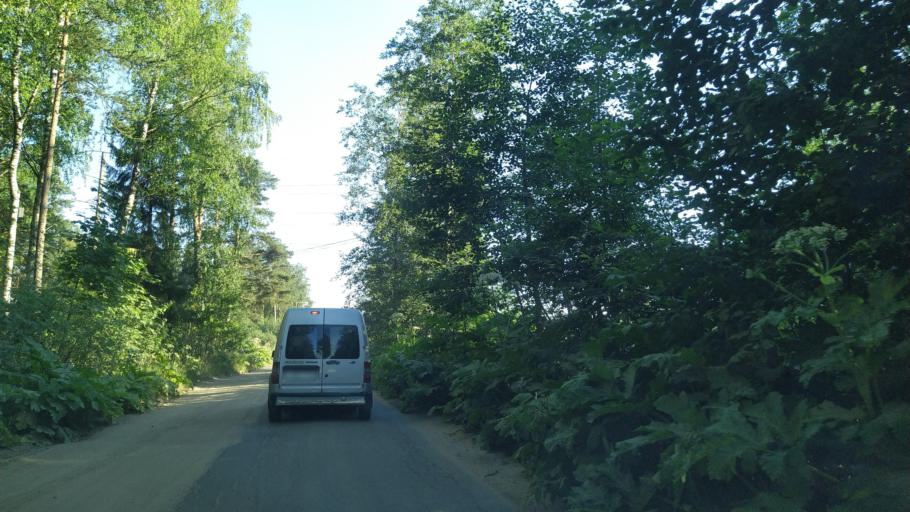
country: RU
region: Leningrad
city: Koltushi
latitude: 59.9025
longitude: 30.7338
